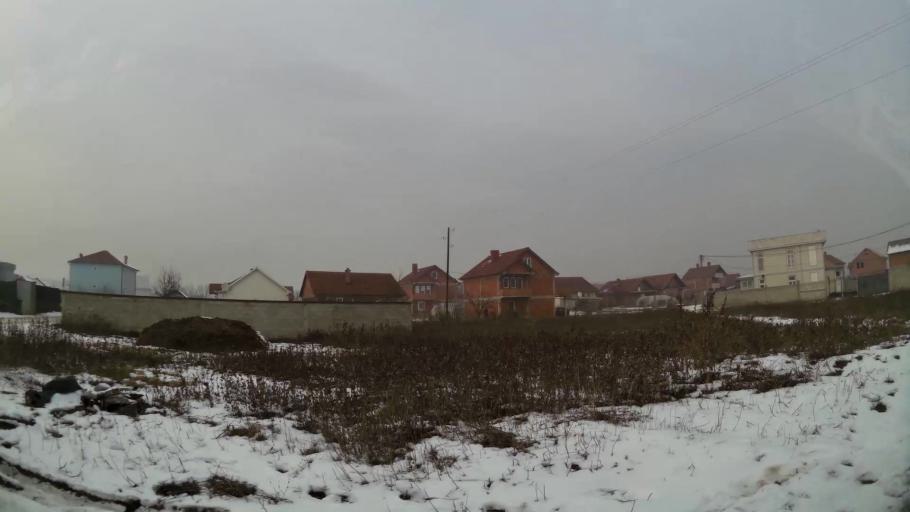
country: MK
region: Suto Orizari
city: Suto Orizare
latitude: 42.0386
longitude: 21.4150
